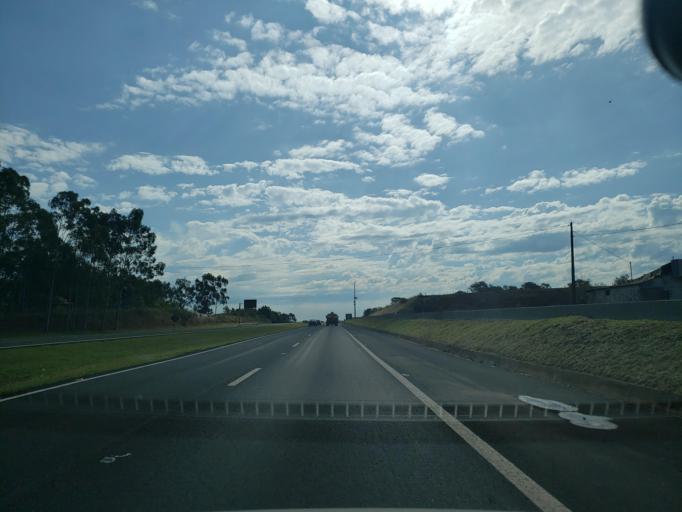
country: BR
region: Sao Paulo
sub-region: Pirajui
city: Pirajui
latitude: -21.9815
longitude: -49.4474
